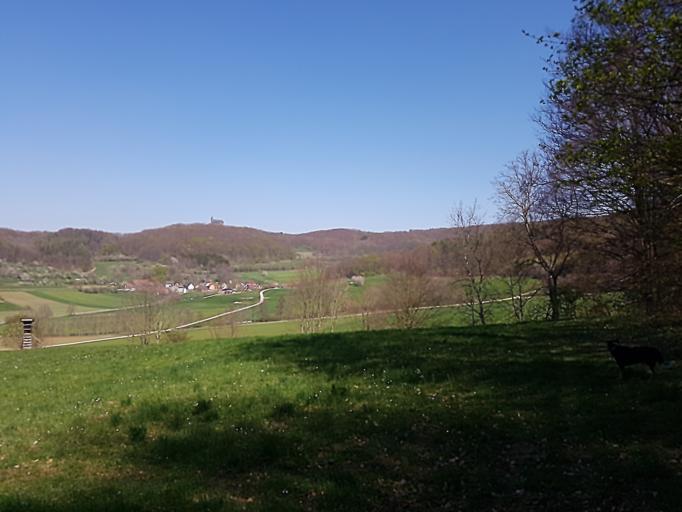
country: DE
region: Bavaria
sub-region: Upper Franconia
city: Schesslitz
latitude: 49.9429
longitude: 11.0466
